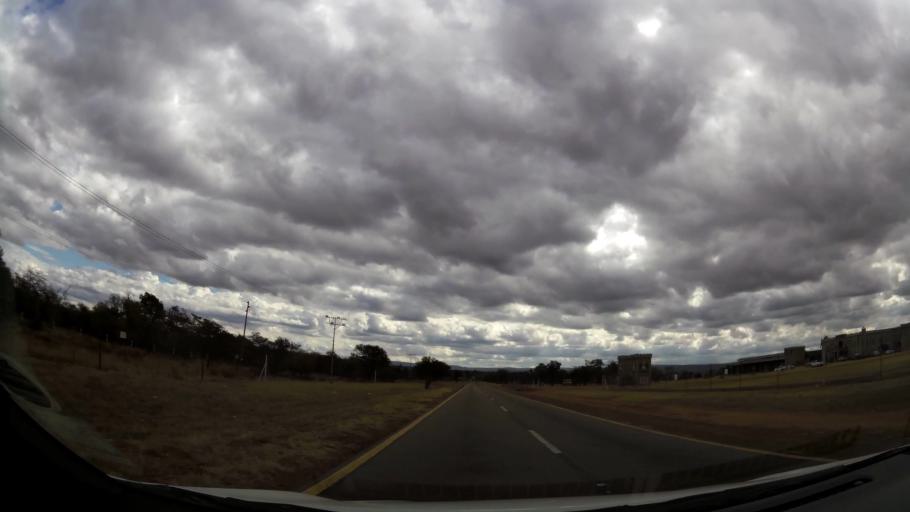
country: ZA
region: Limpopo
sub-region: Waterberg District Municipality
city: Modimolle
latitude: -24.7573
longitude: 28.4528
